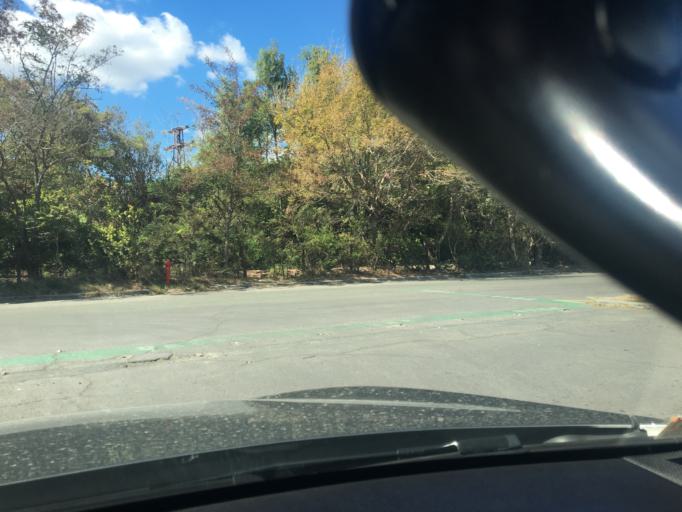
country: BG
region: Burgas
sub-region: Obshtina Burgas
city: Burgas
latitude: 42.5094
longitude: 27.4839
